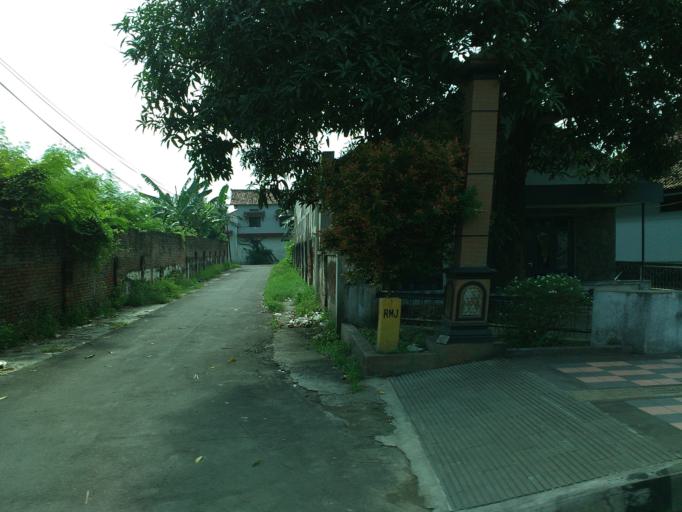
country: ID
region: Central Java
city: Klaten
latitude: -7.6956
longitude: 110.6091
